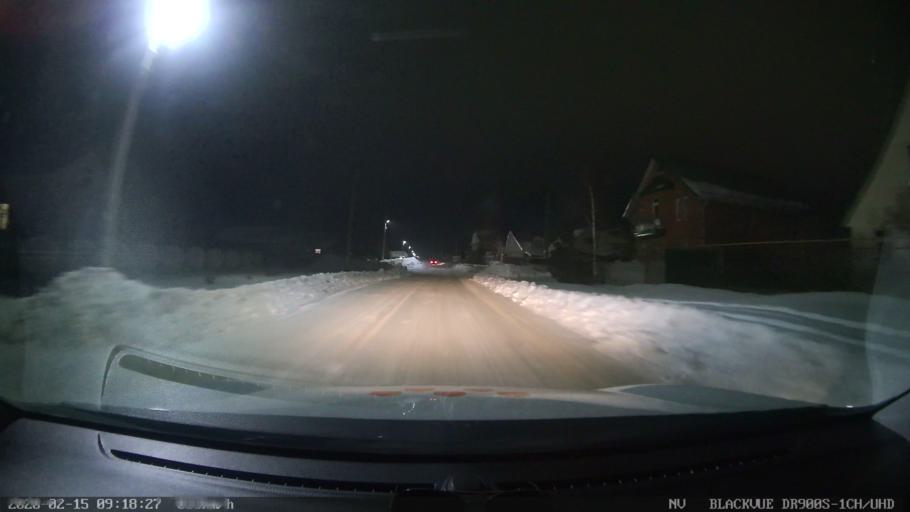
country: RU
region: Tatarstan
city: Stolbishchi
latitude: 55.7167
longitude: 49.3592
